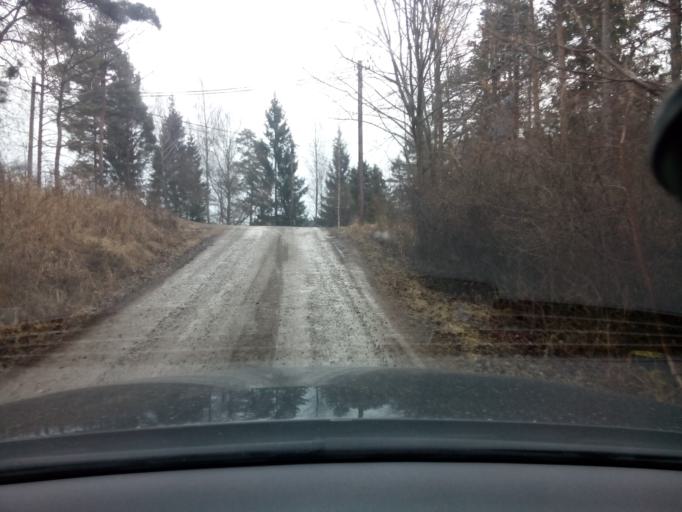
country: SE
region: Soedermanland
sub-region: Trosa Kommun
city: Trosa
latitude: 58.8915
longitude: 17.5772
